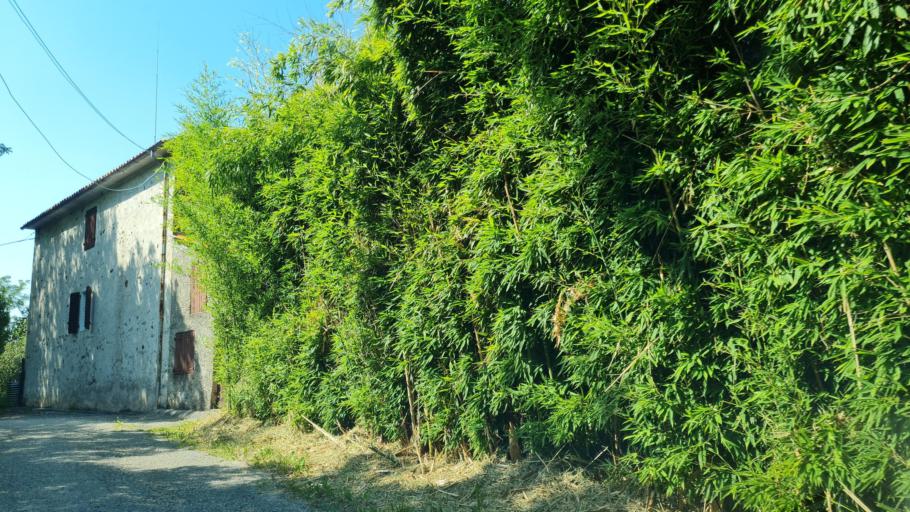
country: IT
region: Veneto
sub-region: Provincia di Vicenza
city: Mure
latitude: 45.7624
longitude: 11.5988
